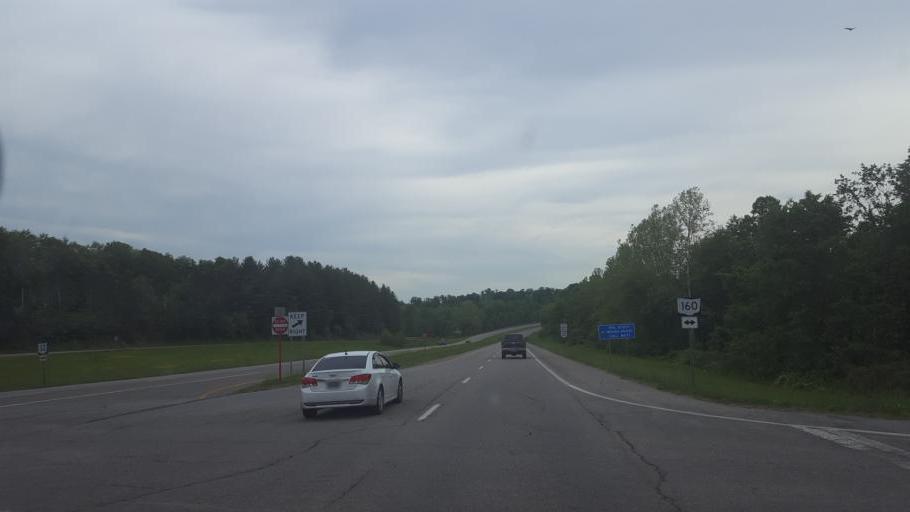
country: US
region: Ohio
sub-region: Vinton County
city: McArthur
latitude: 39.1404
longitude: -82.3728
